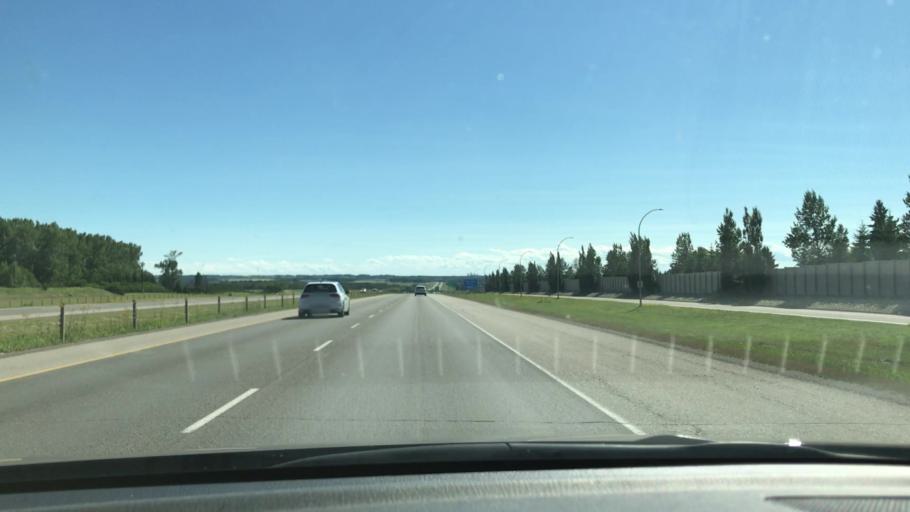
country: CA
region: Alberta
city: Penhold
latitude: 52.0135
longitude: -113.9472
